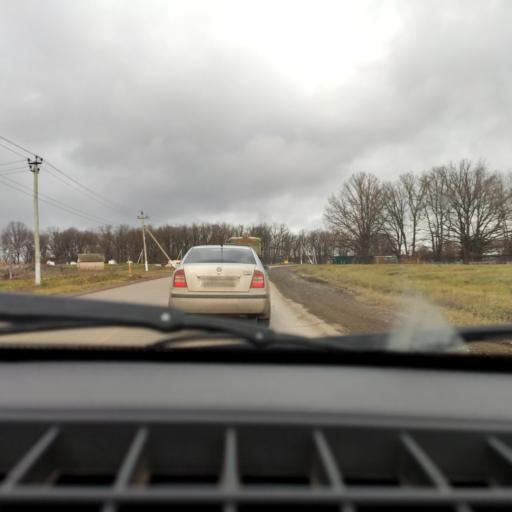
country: RU
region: Bashkortostan
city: Mikhaylovka
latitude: 54.8122
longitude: 55.8823
